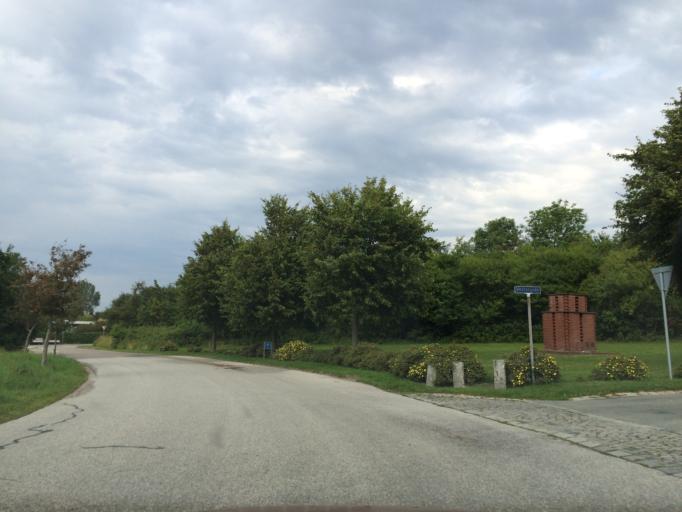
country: DK
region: South Denmark
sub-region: Sonderborg Kommune
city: Broager
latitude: 54.8930
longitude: 9.6692
